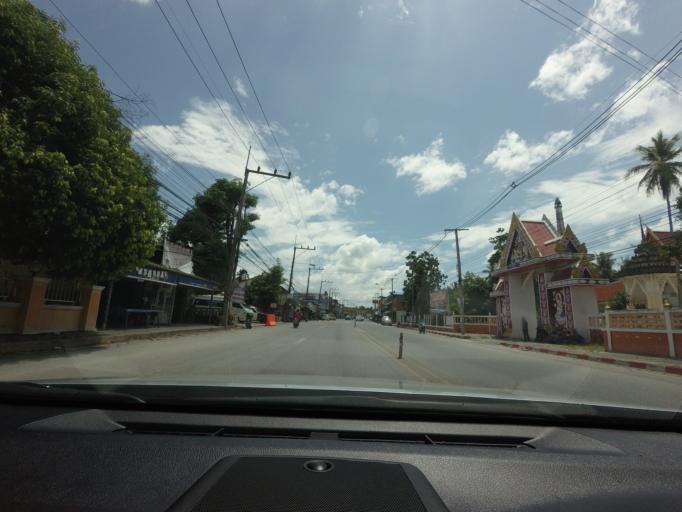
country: TH
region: Nakhon Si Thammarat
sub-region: Amphoe Nopphitam
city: Nopphitam
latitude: 8.9048
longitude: 99.9001
